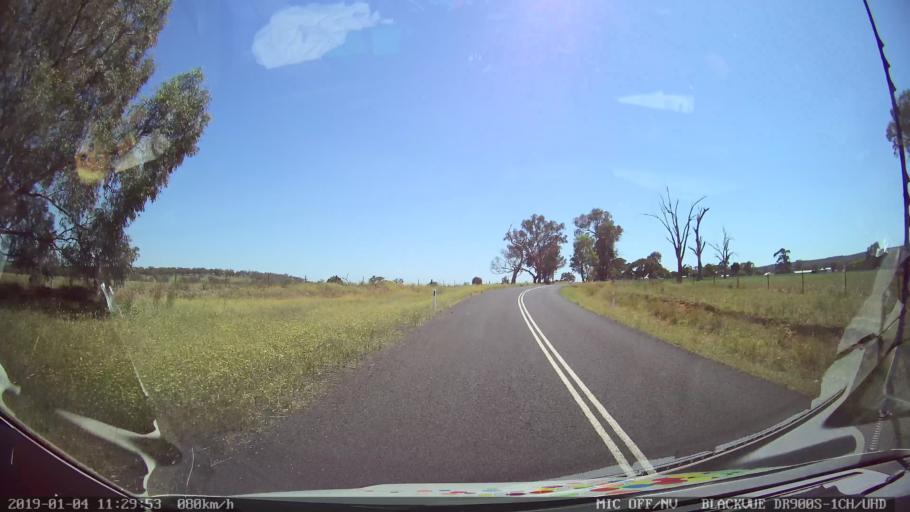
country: AU
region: New South Wales
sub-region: Cabonne
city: Molong
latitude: -33.0826
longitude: 148.7761
